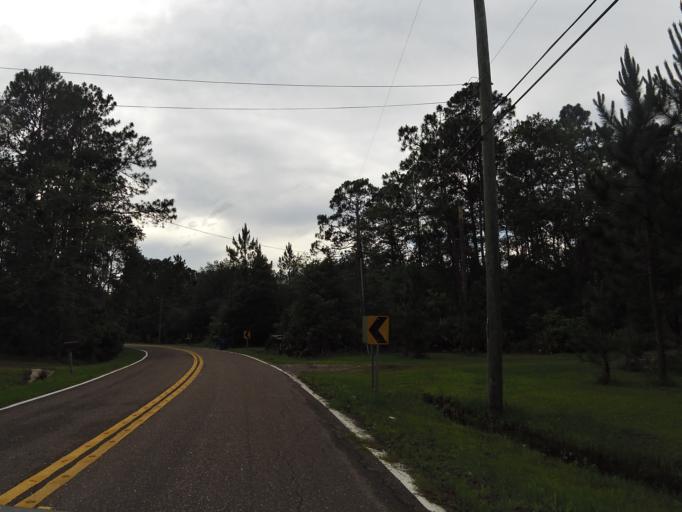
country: US
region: Florida
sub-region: Nassau County
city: Nassau Village-Ratliff
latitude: 30.5498
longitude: -81.6953
